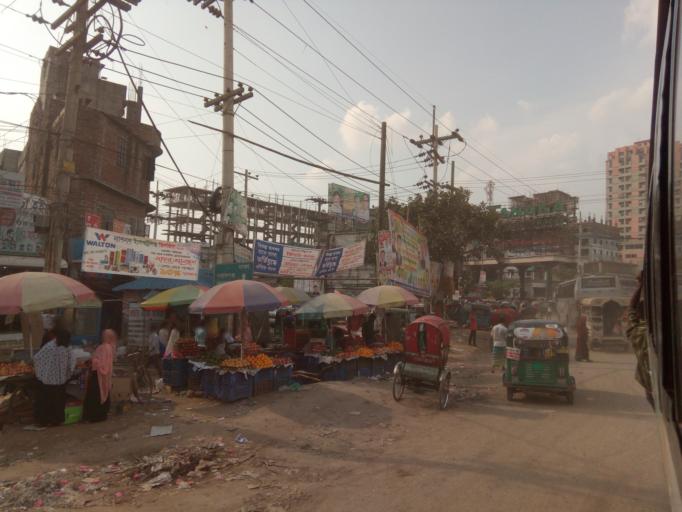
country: BD
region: Dhaka
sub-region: Dhaka
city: Dhaka
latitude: 23.7007
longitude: 90.3975
